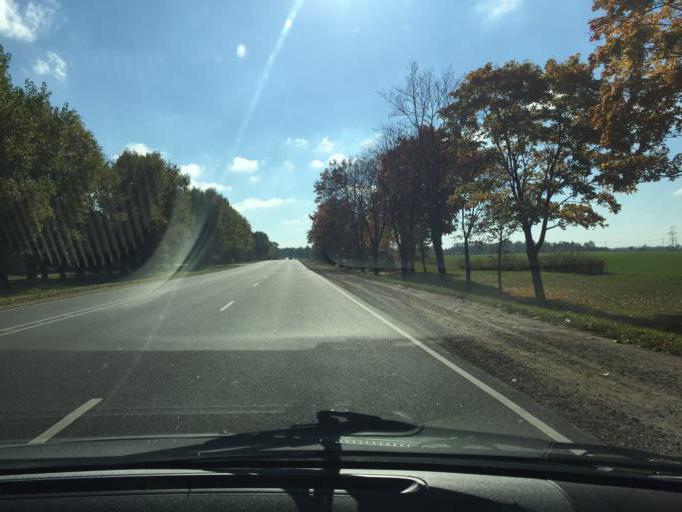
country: BY
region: Minsk
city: Slutsk
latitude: 53.0644
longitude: 27.5536
